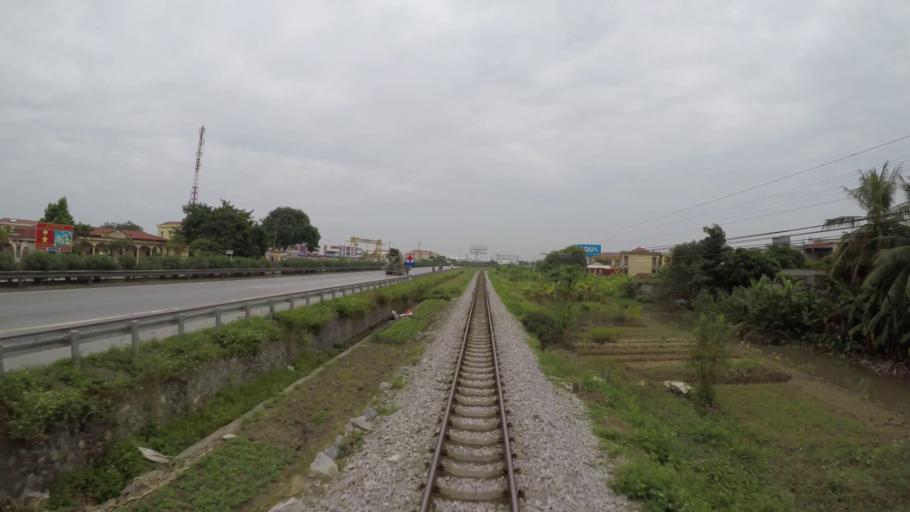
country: VN
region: Hai Duong
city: Nam Sach
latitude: 20.9780
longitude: 106.4135
